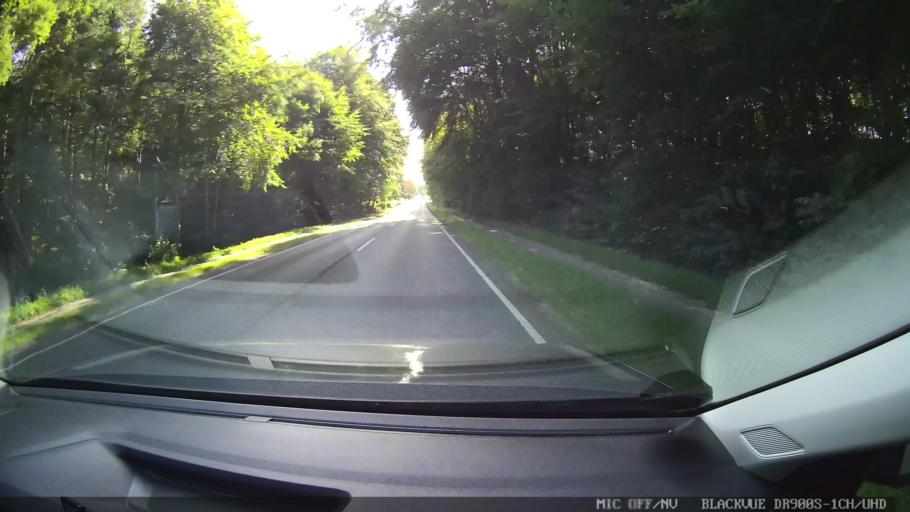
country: DK
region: North Denmark
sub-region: Mariagerfjord Kommune
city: Hadsund
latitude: 56.7226
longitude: 10.0983
